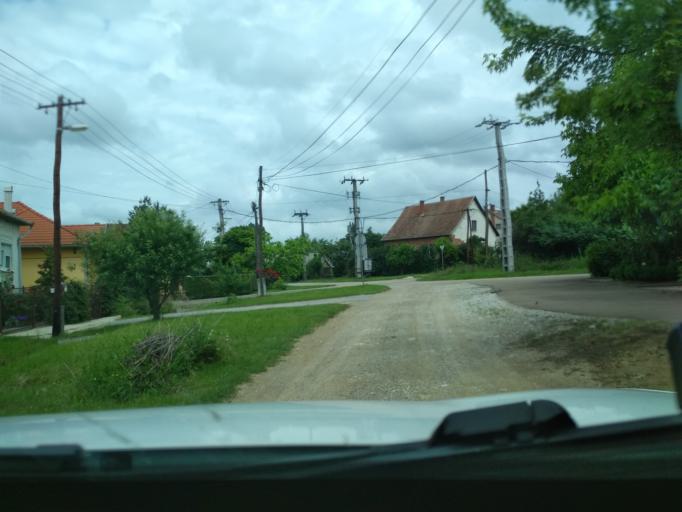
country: HU
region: Jasz-Nagykun-Szolnok
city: Tiszaszolos
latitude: 47.6024
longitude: 20.7209
